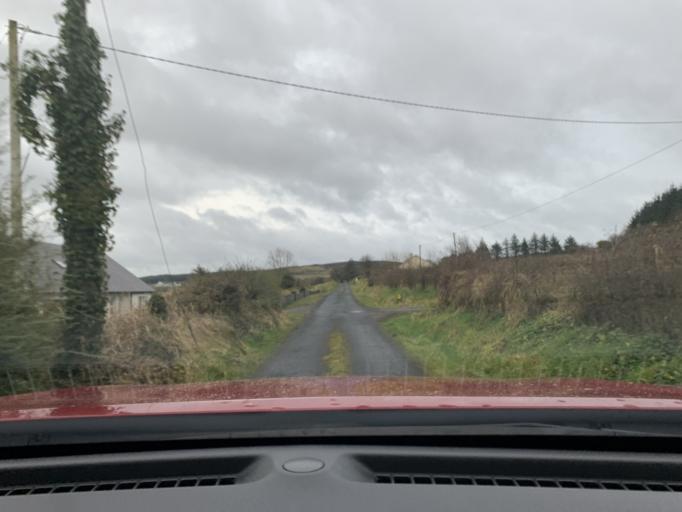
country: IE
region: Connaught
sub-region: Roscommon
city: Ballaghaderreen
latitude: 53.9638
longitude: -8.5013
